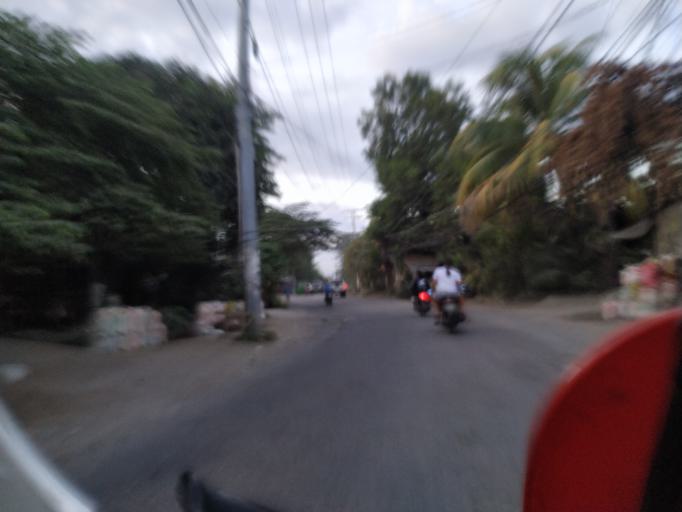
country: PH
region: Central Visayas
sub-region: Province of Negros Oriental
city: Dumaguete
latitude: 9.3060
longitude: 123.2950
